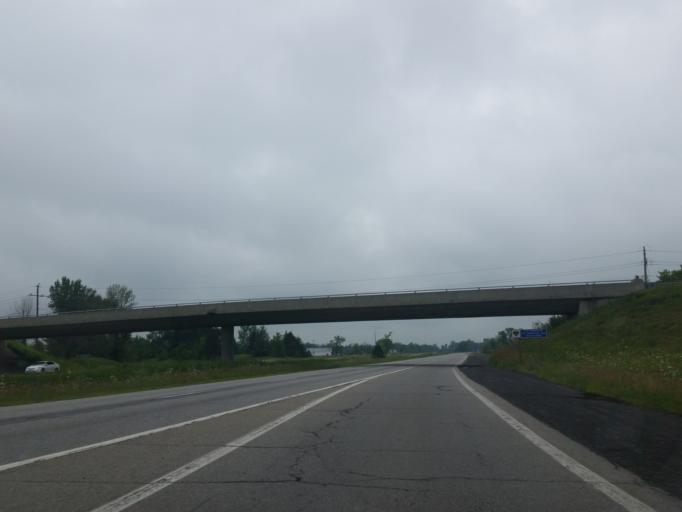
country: CA
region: Ontario
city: Bourget
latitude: 45.3366
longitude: -75.3443
